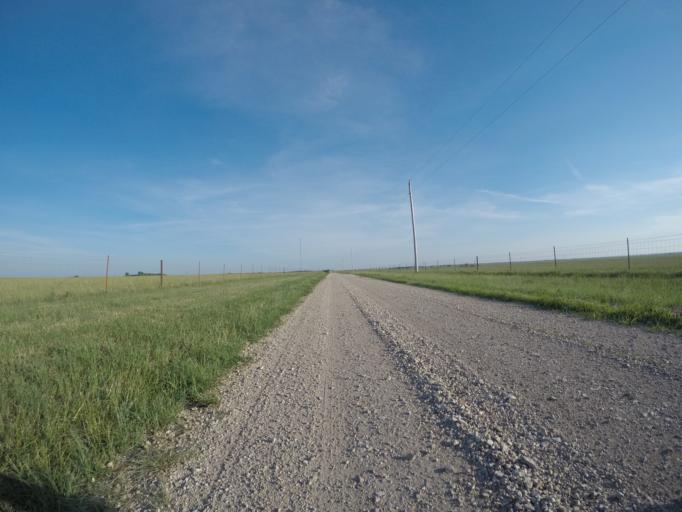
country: US
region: Kansas
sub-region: Riley County
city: Manhattan
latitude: 39.0106
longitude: -96.4919
